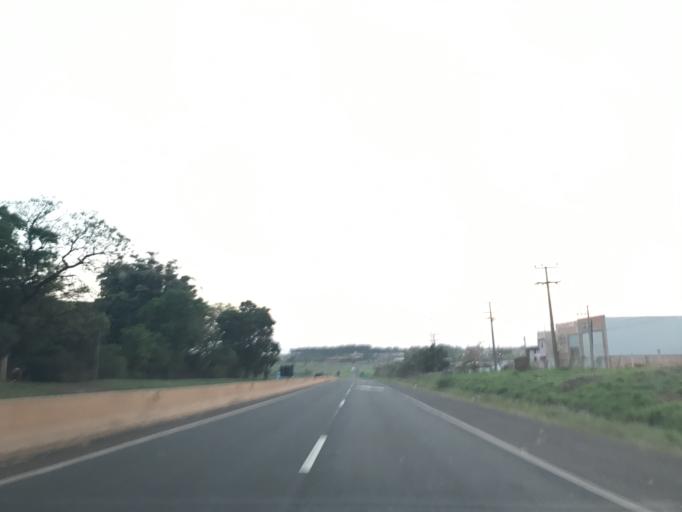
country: BR
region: Sao Paulo
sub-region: Assis
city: Assis
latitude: -22.6415
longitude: -50.4388
